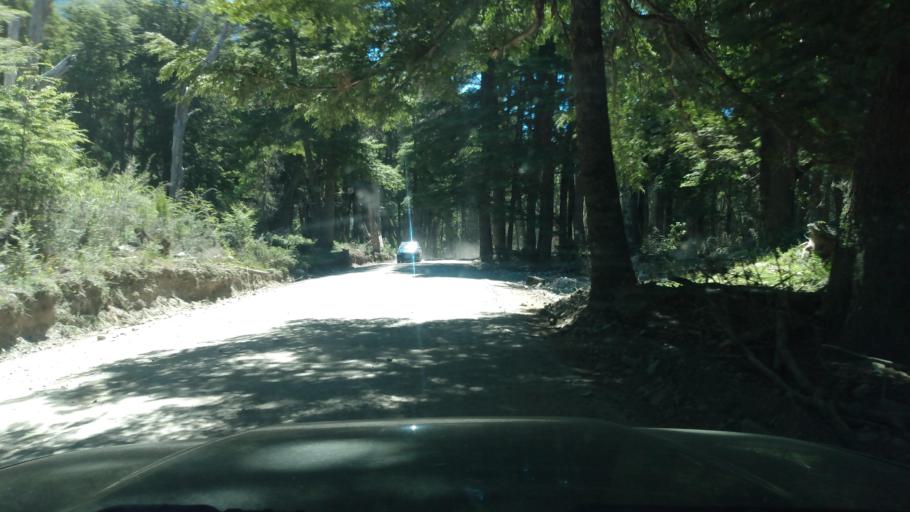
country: AR
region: Neuquen
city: Villa La Angostura
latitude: -40.6239
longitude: -71.5930
